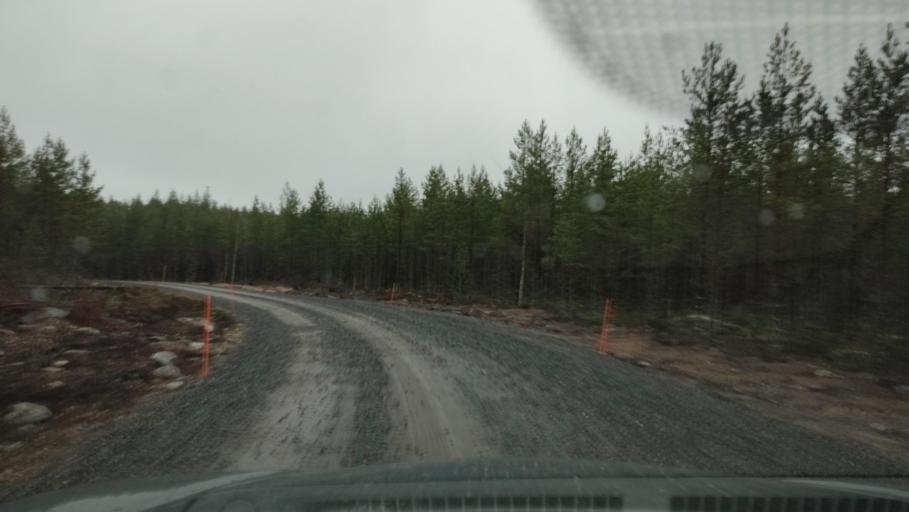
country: FI
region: Southern Ostrobothnia
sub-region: Suupohja
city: Karijoki
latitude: 62.1478
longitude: 21.6258
